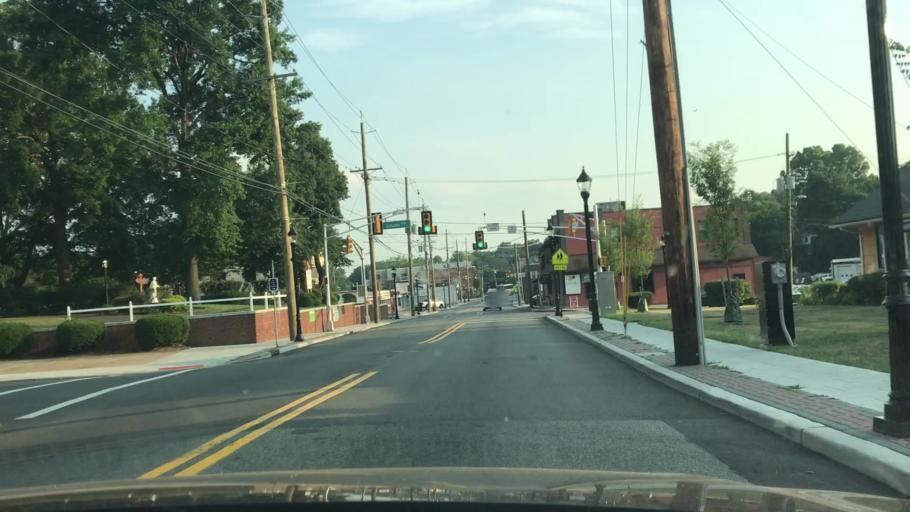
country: US
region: New Jersey
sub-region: Bergen County
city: Emerson
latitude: 40.9773
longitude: -74.0257
